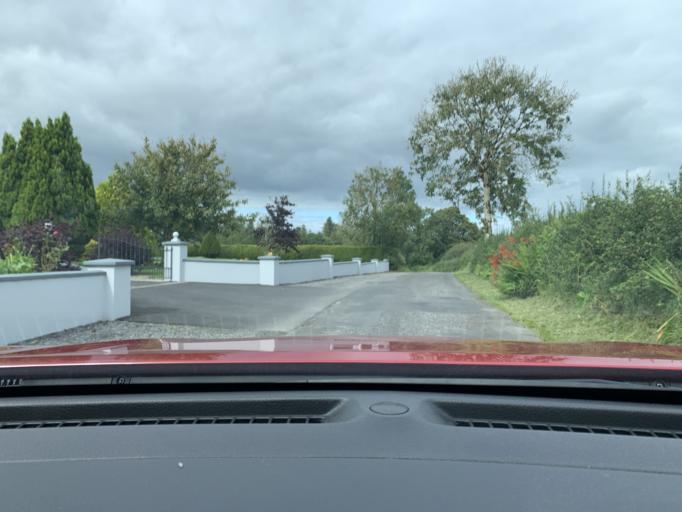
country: IE
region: Connaught
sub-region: Sligo
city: Collooney
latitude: 54.1549
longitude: -8.4266
